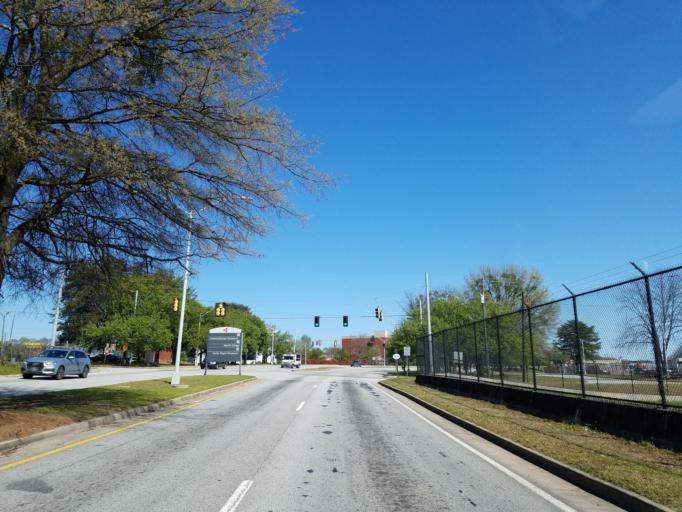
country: US
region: Georgia
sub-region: Fulton County
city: Hapeville
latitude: 33.6578
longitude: -84.4197
